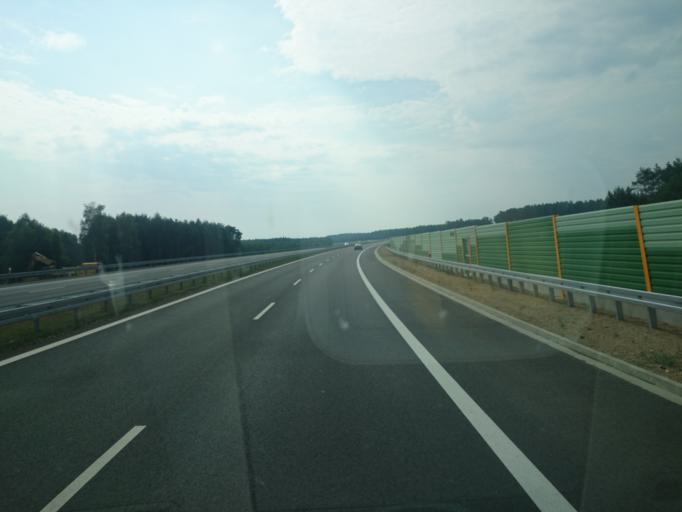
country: PL
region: Lubusz
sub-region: Powiat gorzowski
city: Deszczno
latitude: 52.6538
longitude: 15.3391
